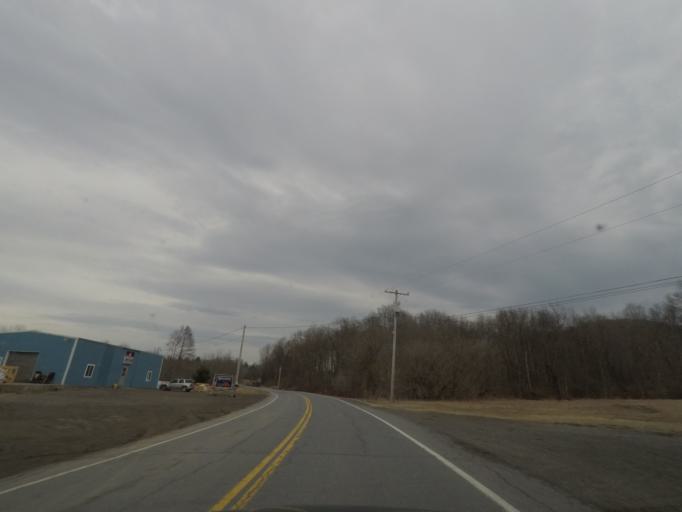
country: US
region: New York
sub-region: Washington County
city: Greenwich
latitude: 43.0431
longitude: -73.4966
